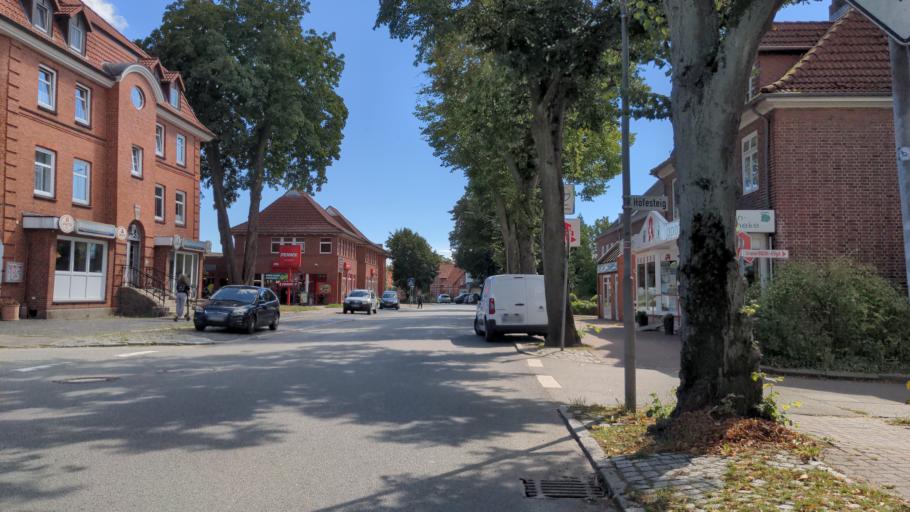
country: DE
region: Schleswig-Holstein
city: Lensahn
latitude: 54.2197
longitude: 10.8880
